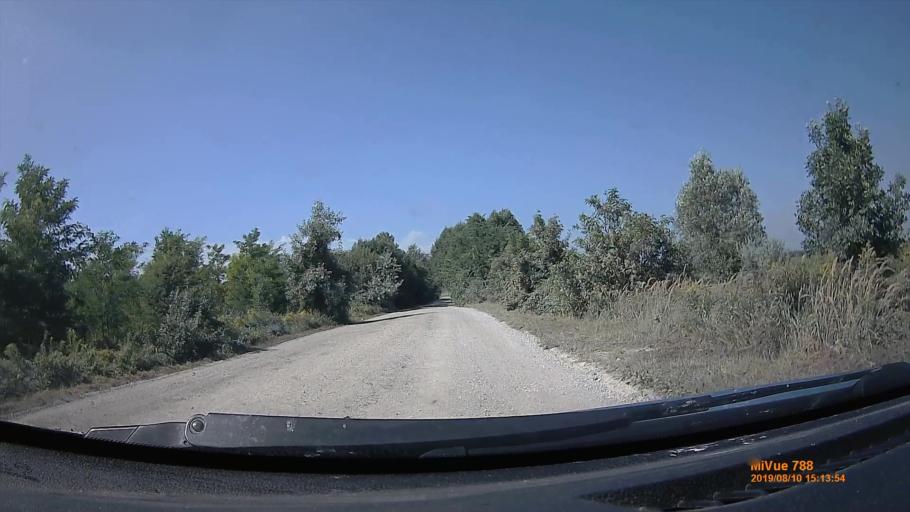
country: HU
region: Somogy
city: Fonyod
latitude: 46.6943
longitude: 17.5596
